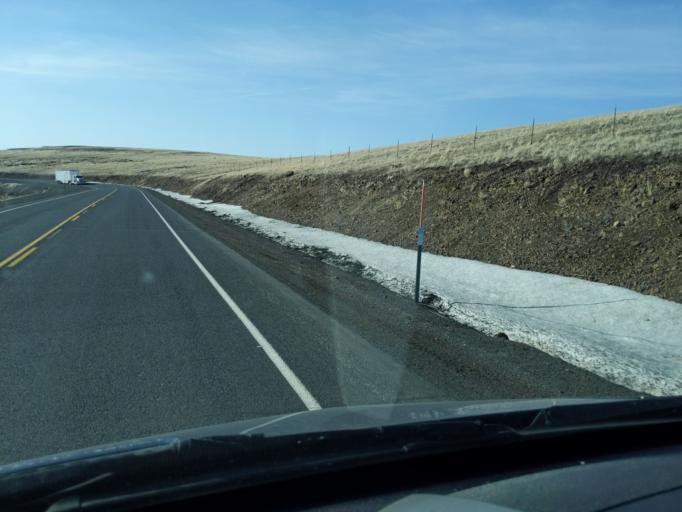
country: US
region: Oregon
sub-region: Umatilla County
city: Pilot Rock
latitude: 45.3002
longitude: -118.9949
